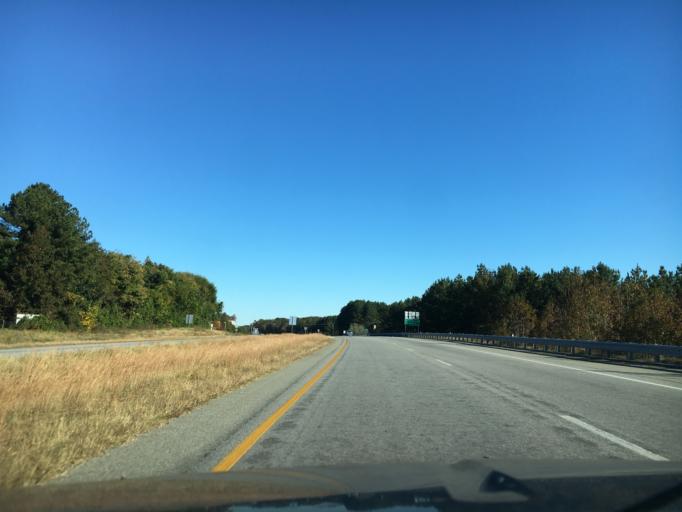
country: US
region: Virginia
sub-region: Mecklenburg County
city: Clarksville
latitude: 36.6124
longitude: -78.5922
